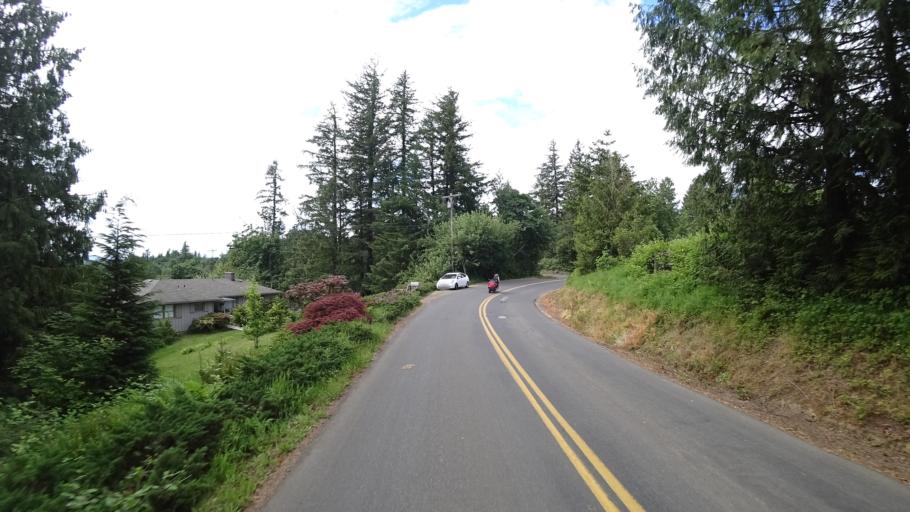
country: US
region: Oregon
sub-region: Washington County
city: Bethany
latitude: 45.6101
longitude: -122.8315
